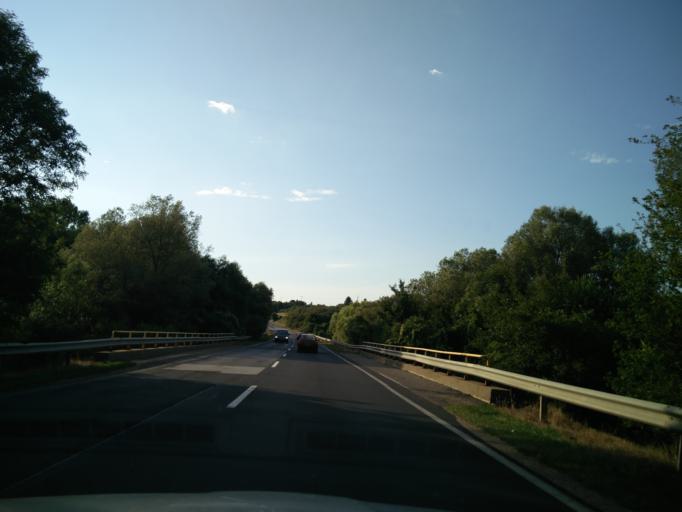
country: HU
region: Veszprem
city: Veszprem
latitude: 47.0961
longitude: 17.8748
